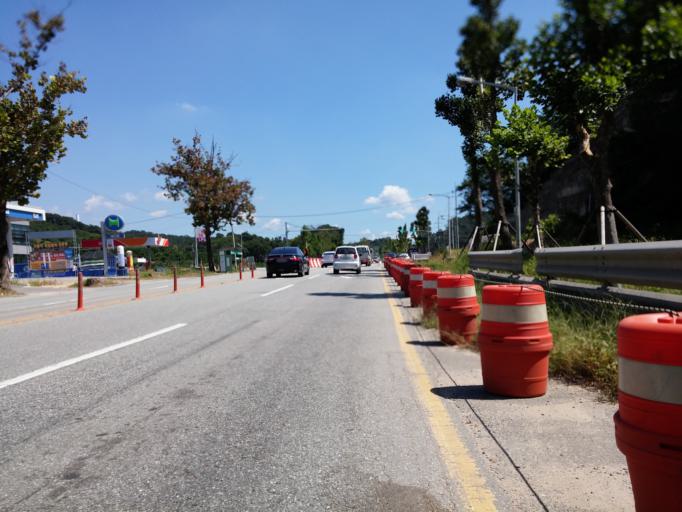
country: KR
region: Chungcheongbuk-do
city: Cheongju-si
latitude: 36.6201
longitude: 127.3866
